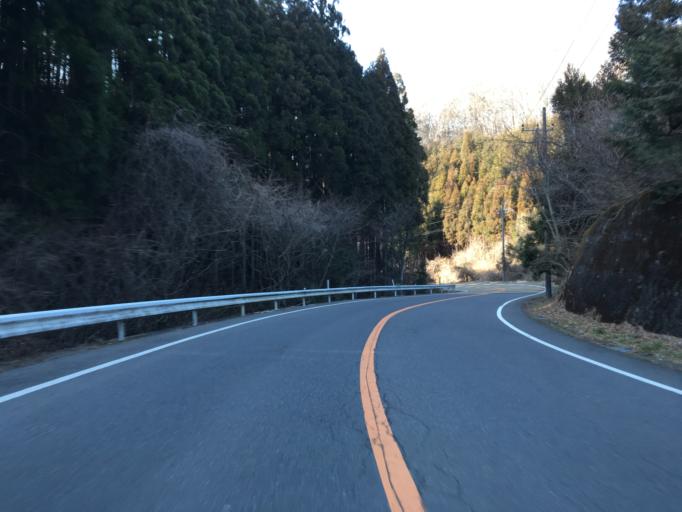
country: JP
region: Ibaraki
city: Takahagi
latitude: 36.7368
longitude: 140.5544
